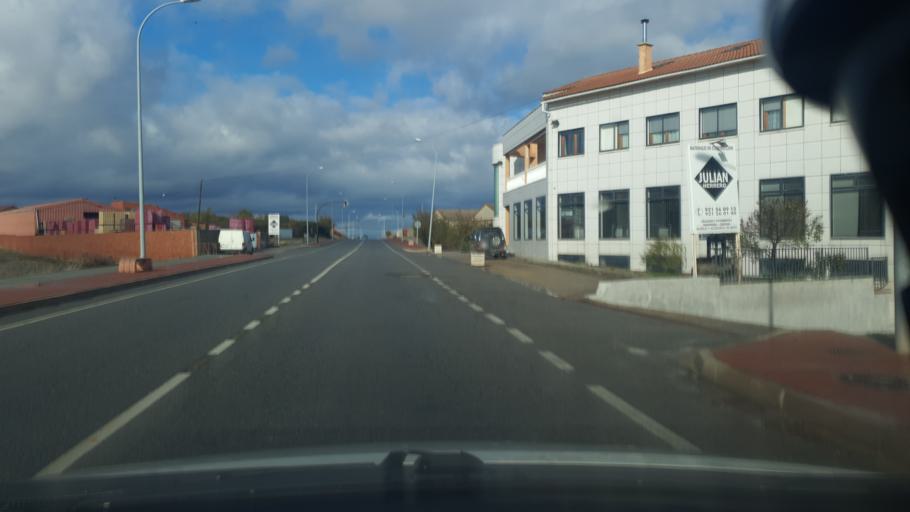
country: ES
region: Castille and Leon
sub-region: Provincia de Segovia
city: Carbonero el Mayor
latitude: 41.1252
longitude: -4.2685
